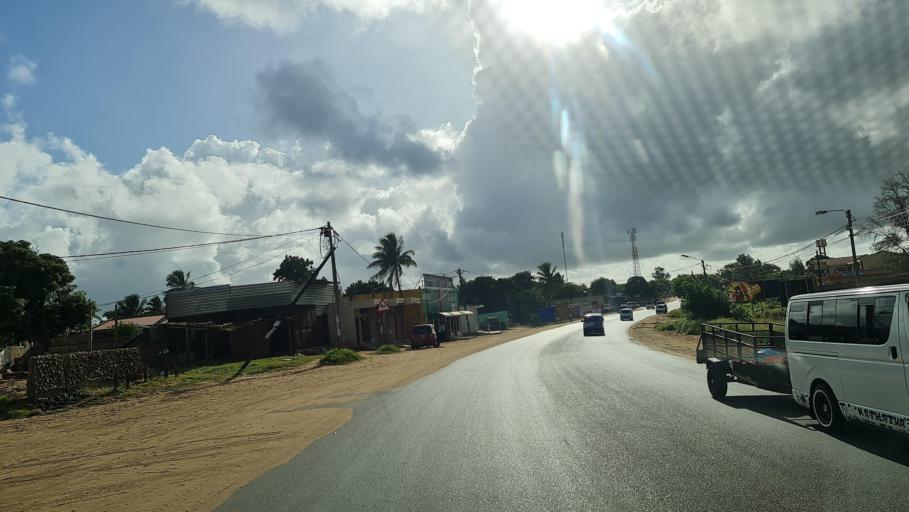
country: MZ
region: Gaza
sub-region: Xai-Xai District
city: Xai-Xai
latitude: -25.0555
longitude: 33.6676
